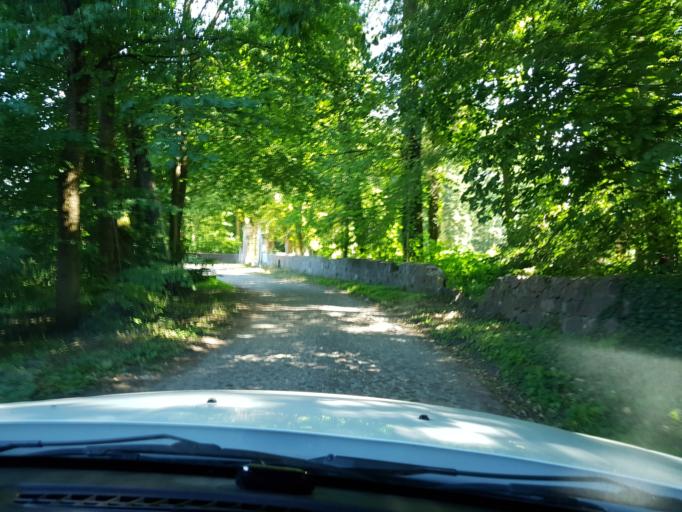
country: PL
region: West Pomeranian Voivodeship
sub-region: Powiat bialogardzki
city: Karlino
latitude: 53.9323
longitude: 15.8266
